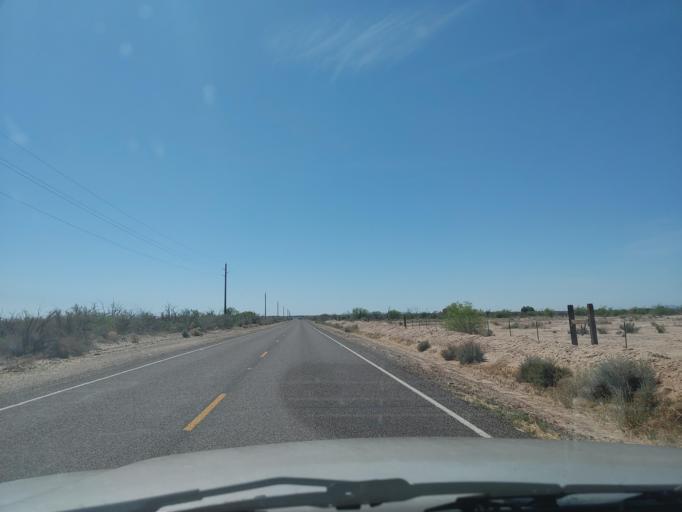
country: US
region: Arizona
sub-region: Maricopa County
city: Gila Bend
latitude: 32.9771
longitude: -113.3060
